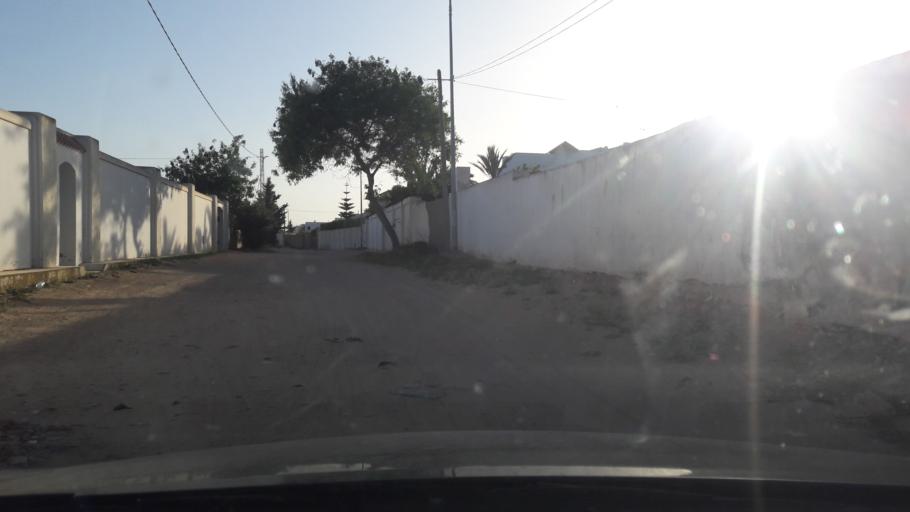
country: TN
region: Safaqis
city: Al Qarmadah
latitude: 34.7954
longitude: 10.7564
